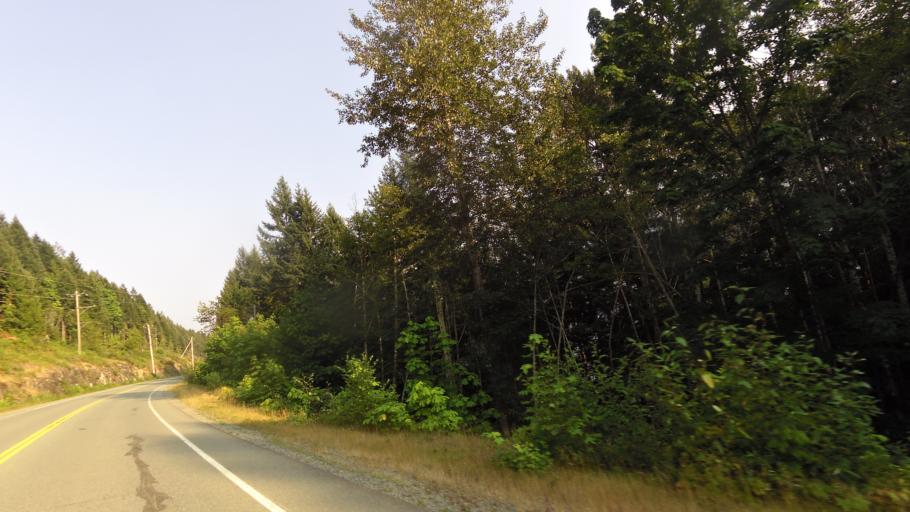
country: CA
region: British Columbia
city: Port Alberni
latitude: 49.2786
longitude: -125.0625
